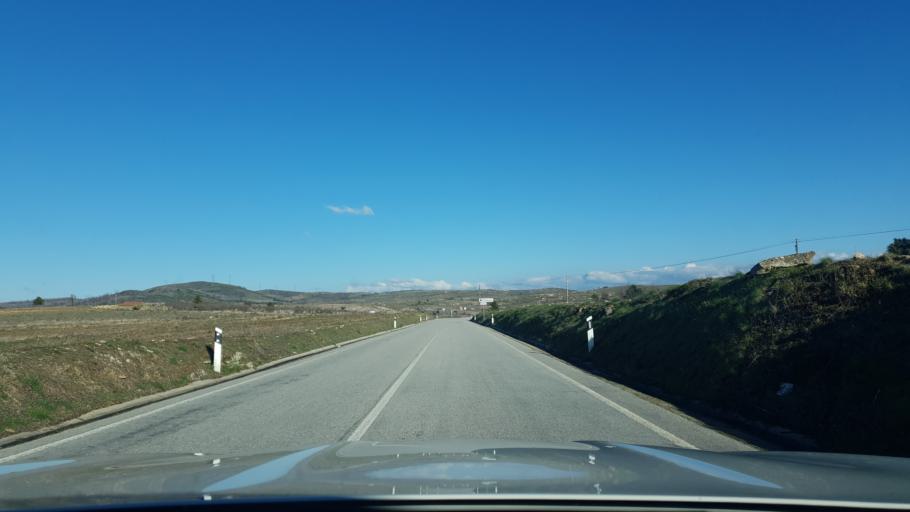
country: PT
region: Braganca
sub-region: Freixo de Espada A Cinta
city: Freixo de Espada a Cinta
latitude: 41.1847
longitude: -6.8286
